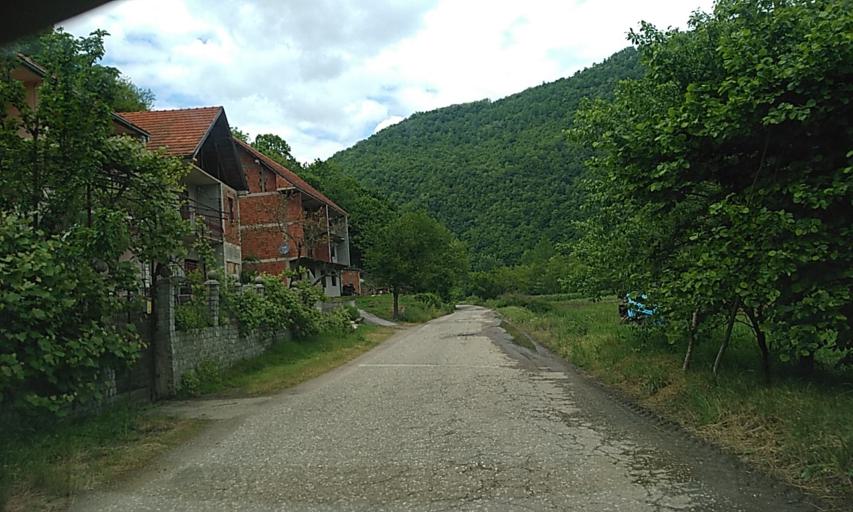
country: RS
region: Central Serbia
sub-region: Pcinjski Okrug
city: Vladicin Han
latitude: 42.7288
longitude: 22.0631
